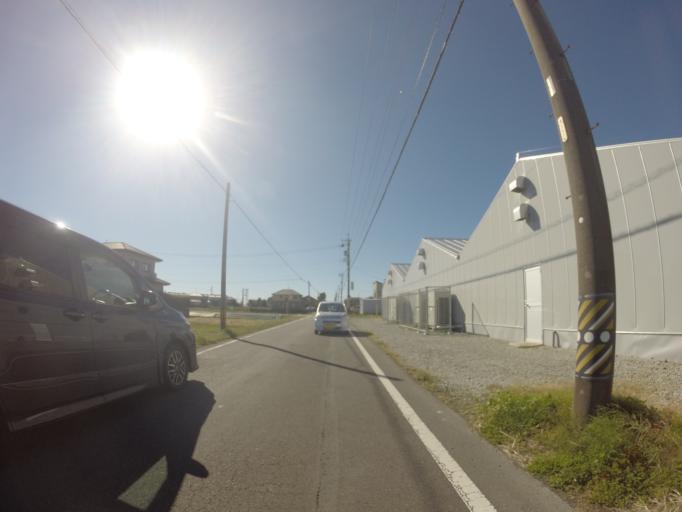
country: JP
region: Shizuoka
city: Fujieda
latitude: 34.8352
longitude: 138.2392
